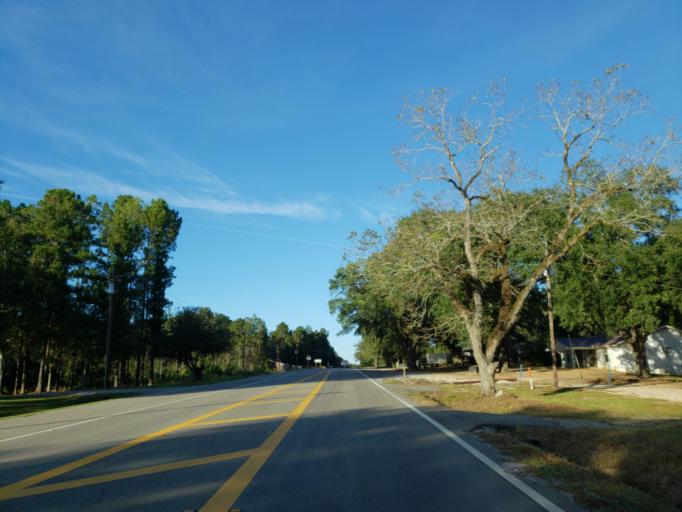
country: US
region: Mississippi
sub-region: Perry County
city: Richton
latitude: 31.3504
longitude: -88.7612
